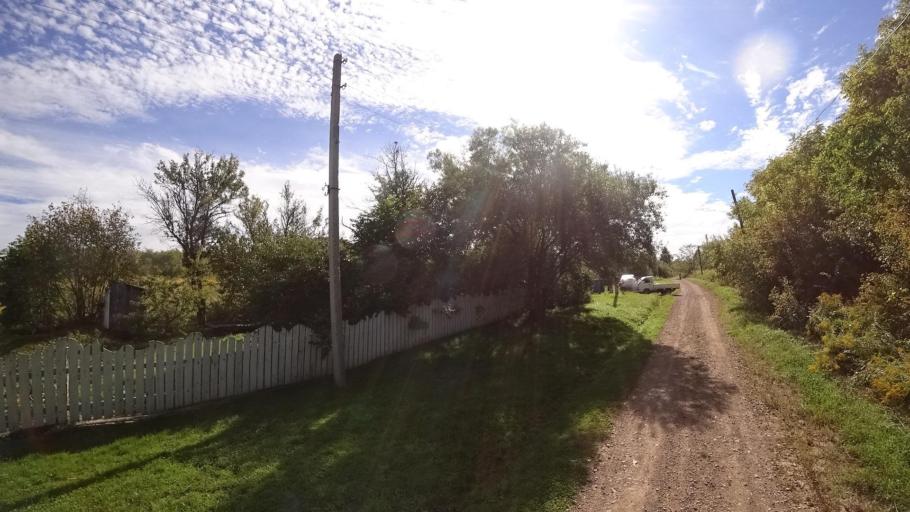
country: RU
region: Primorskiy
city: Yakovlevka
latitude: 44.3897
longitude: 133.6049
